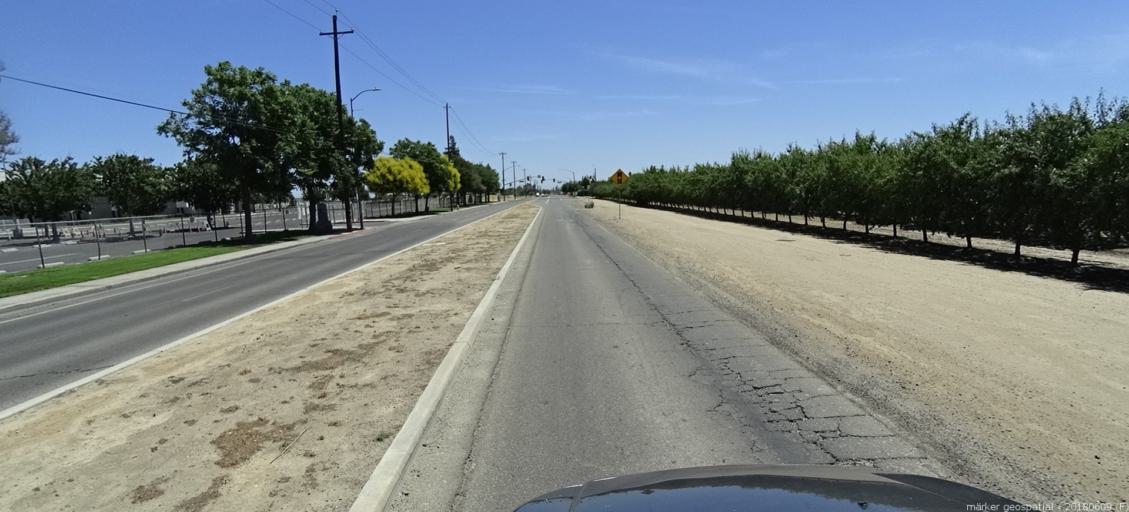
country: US
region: California
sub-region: Madera County
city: Madera
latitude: 36.9383
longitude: -120.0673
